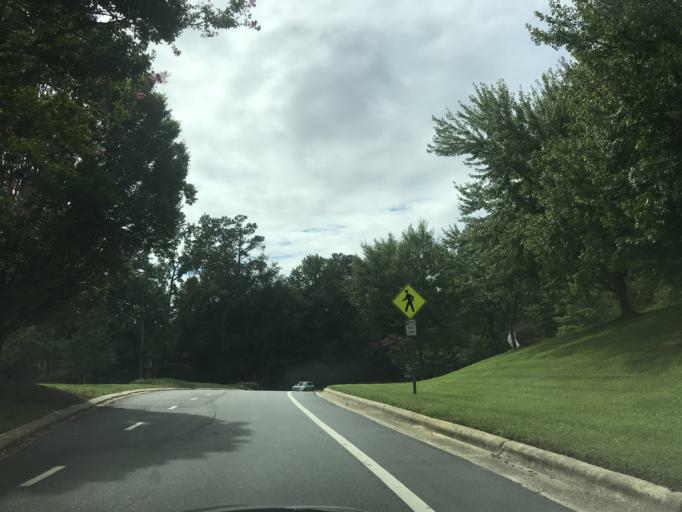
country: US
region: North Carolina
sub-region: Wake County
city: Cary
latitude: 35.7291
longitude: -78.7793
